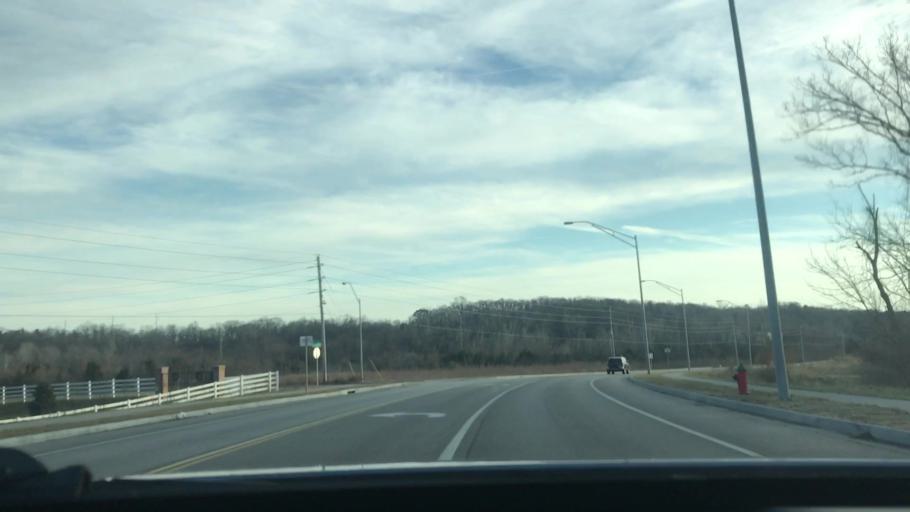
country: US
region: Missouri
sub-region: Jackson County
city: Raytown
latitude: 39.0169
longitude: -94.3871
